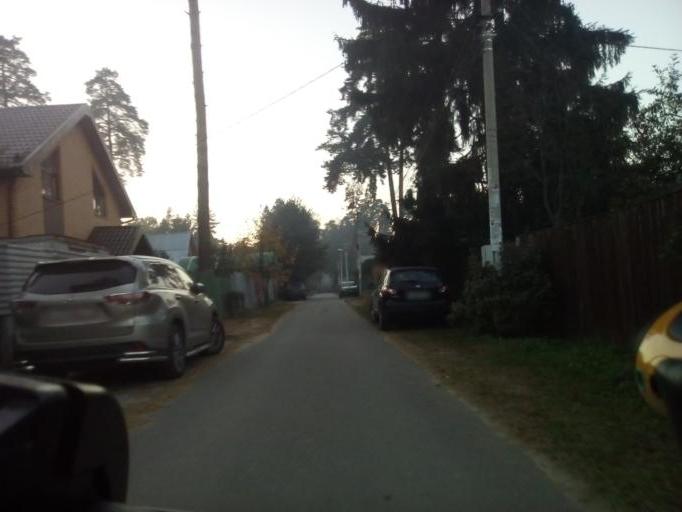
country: RU
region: Moskovskaya
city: Kratovo
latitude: 55.6022
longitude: 38.1799
